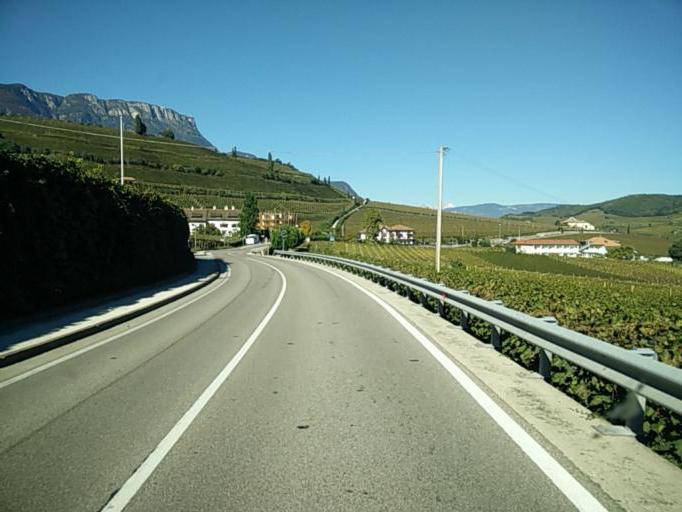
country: IT
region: Trentino-Alto Adige
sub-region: Bolzano
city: Caldaro sulla Strada del Vino
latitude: 46.3832
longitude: 11.2544
